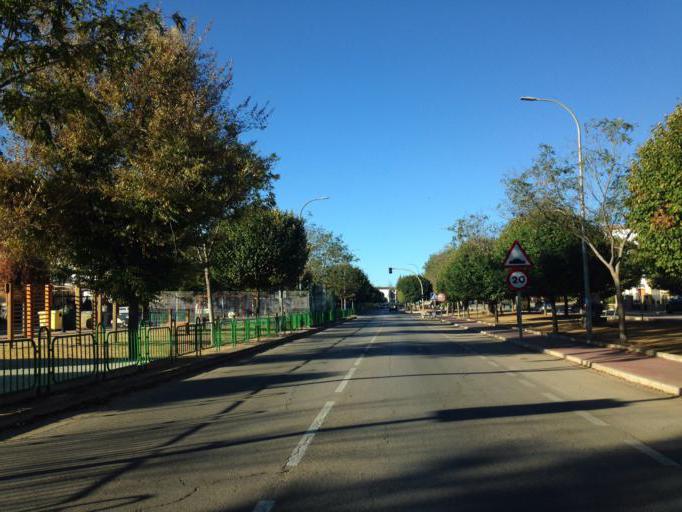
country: ES
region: Andalusia
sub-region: Provincia de Malaga
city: Archidona
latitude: 37.0967
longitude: -4.3746
